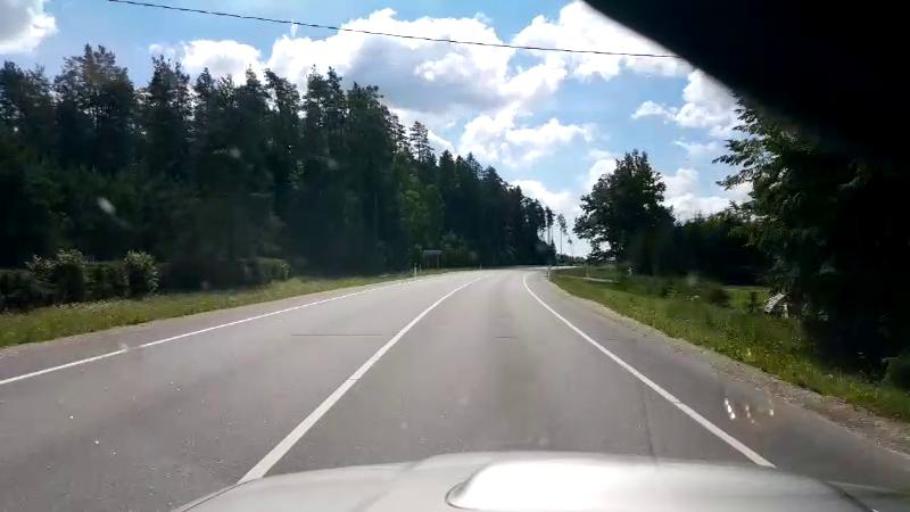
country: EE
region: Jaervamaa
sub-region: Jaerva-Jaani vald
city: Jarva-Jaani
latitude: 59.0492
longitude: 25.7065
